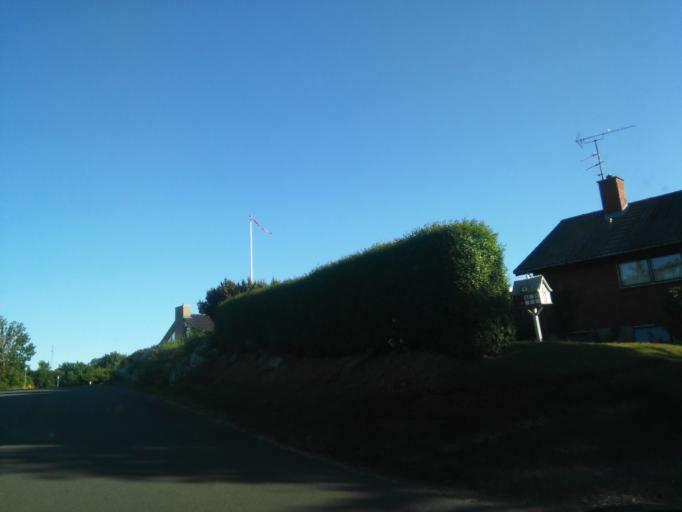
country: DK
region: Capital Region
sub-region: Bornholm Kommune
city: Ronne
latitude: 55.2722
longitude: 14.8033
